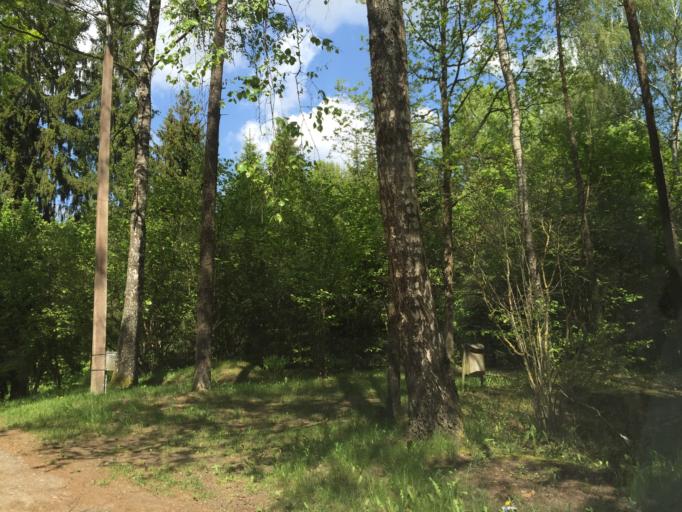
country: LV
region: Baldone
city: Baldone
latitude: 56.7375
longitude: 24.3644
